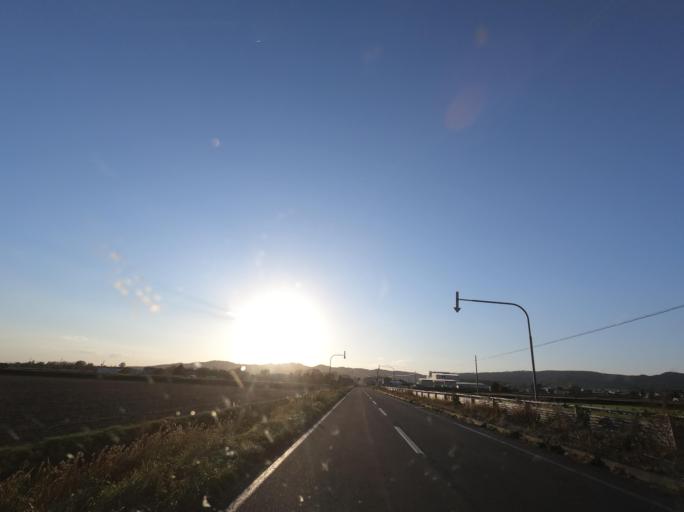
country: JP
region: Hokkaido
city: Chitose
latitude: 42.9748
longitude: 141.7999
